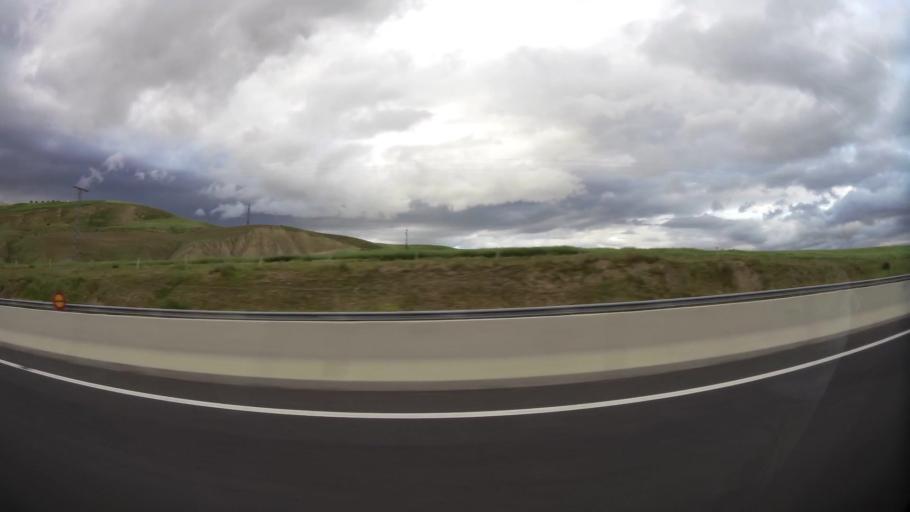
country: MA
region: Taza-Al Hoceima-Taounate
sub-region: Taza
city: Taza
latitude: 34.2588
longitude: -3.9376
